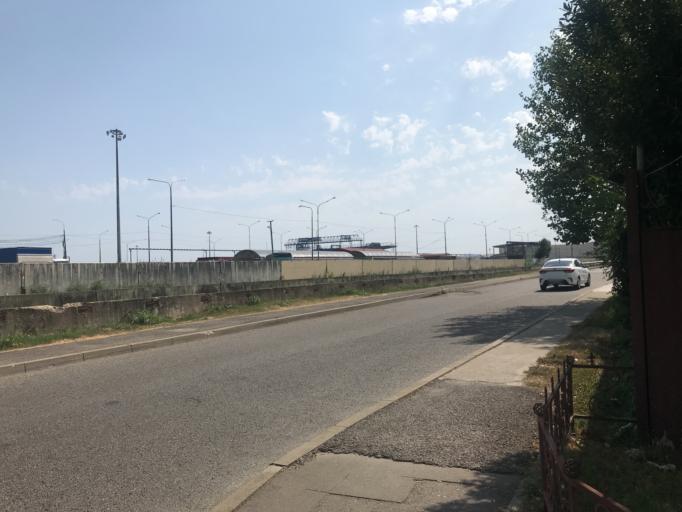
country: RU
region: Krasnodarskiy
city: Vysokoye
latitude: 43.4034
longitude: 39.9873
